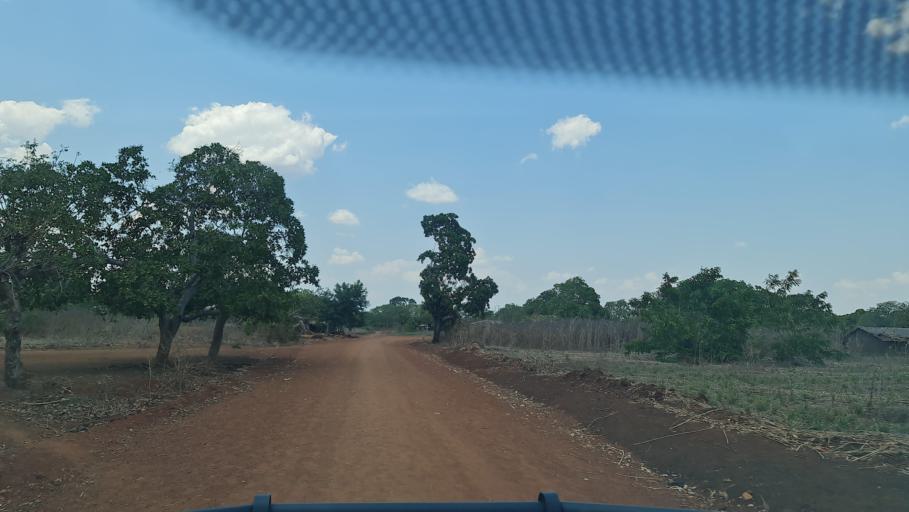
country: MZ
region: Nampula
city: Nacala
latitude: -14.8122
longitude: 40.0743
